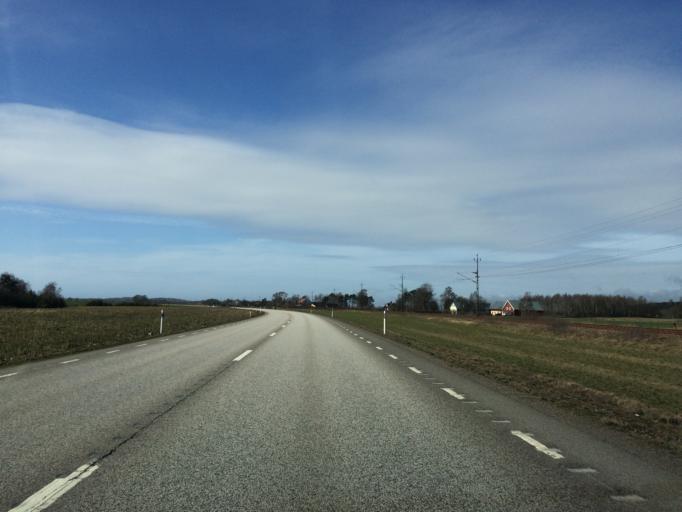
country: SE
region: Halland
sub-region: Laholms Kommun
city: Veinge
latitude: 56.5396
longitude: 13.1532
